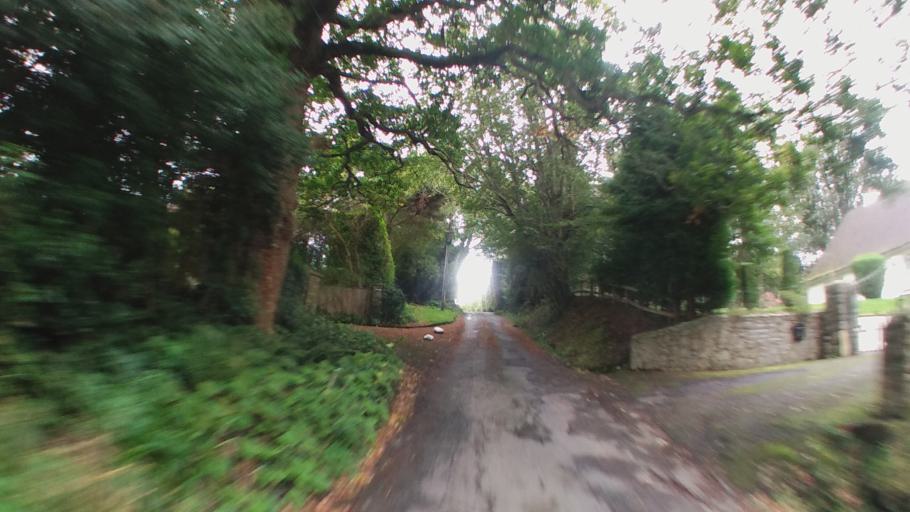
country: IE
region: Leinster
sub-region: Wicklow
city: Enniskerry
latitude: 53.1736
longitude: -6.2162
